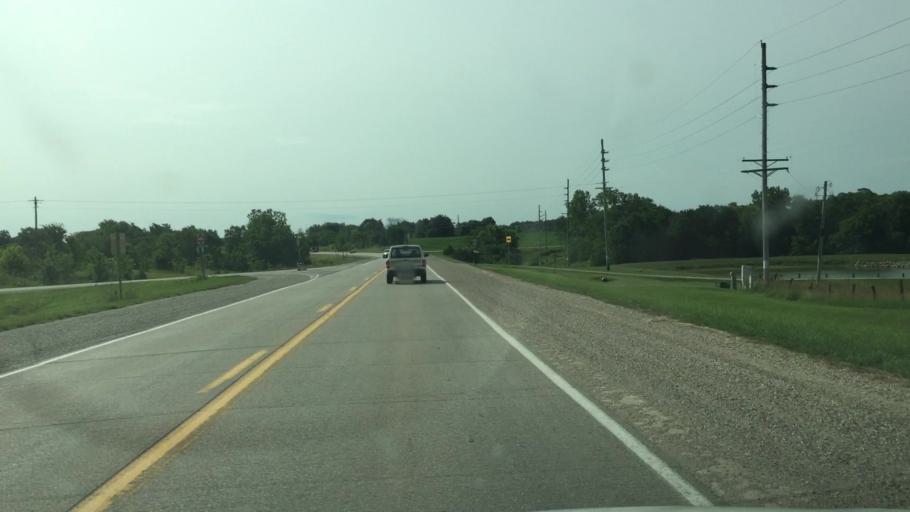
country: US
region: Illinois
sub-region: Hancock County
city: Nauvoo
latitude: 40.6357
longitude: -91.5179
